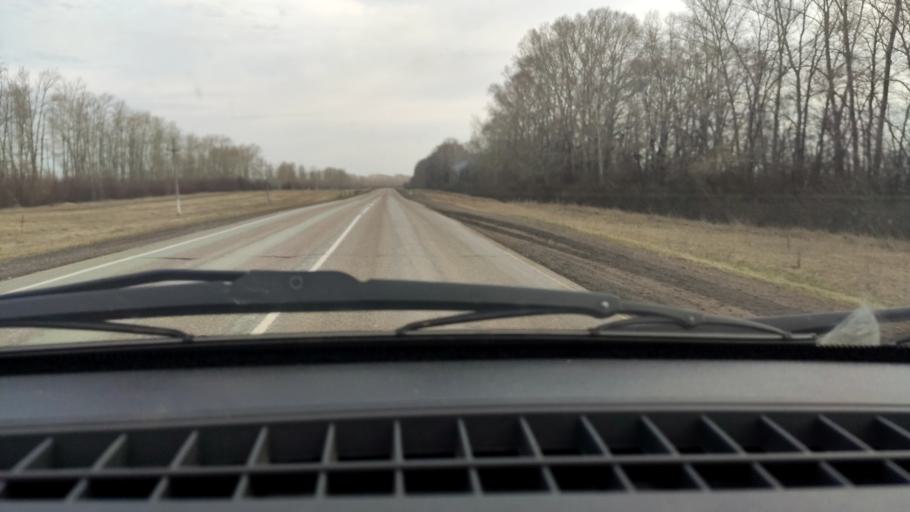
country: RU
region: Bashkortostan
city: Davlekanovo
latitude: 54.3411
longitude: 55.1727
